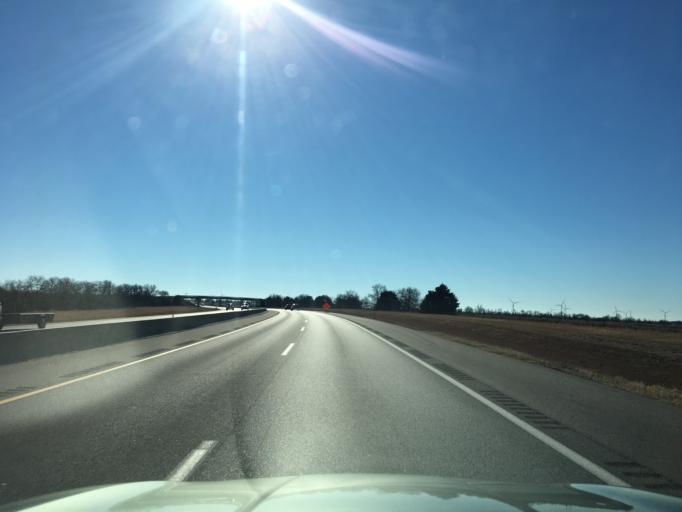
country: US
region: Kansas
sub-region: Sumner County
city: Wellington
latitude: 37.1928
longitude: -97.3418
